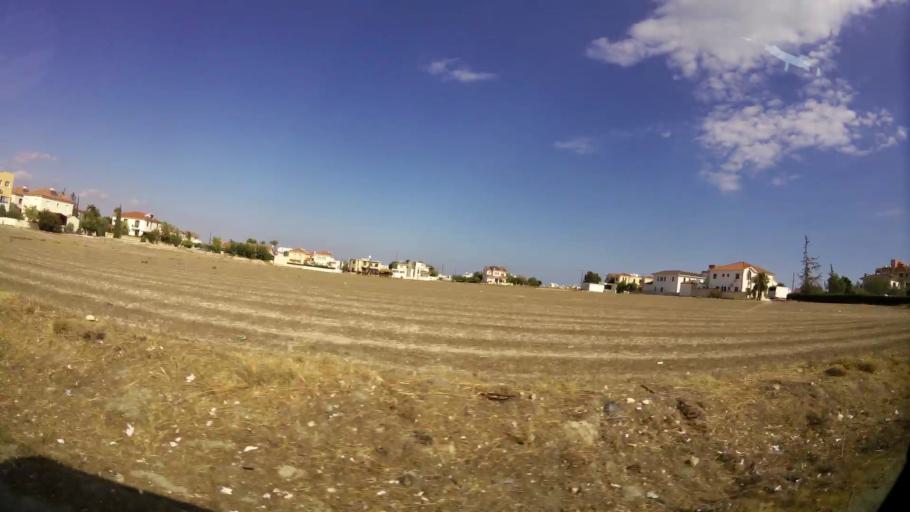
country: CY
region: Larnaka
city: Livadia
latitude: 34.9409
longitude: 33.6183
